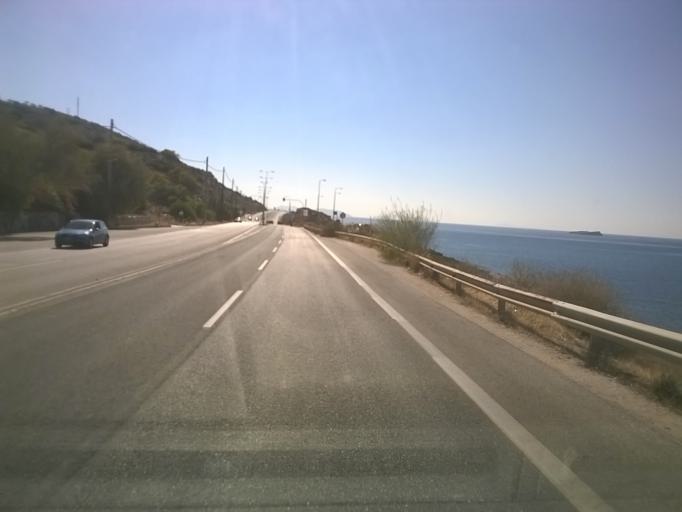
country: GR
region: Attica
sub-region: Nomarchia Anatolikis Attikis
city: Vari
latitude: 37.8161
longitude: 23.8203
